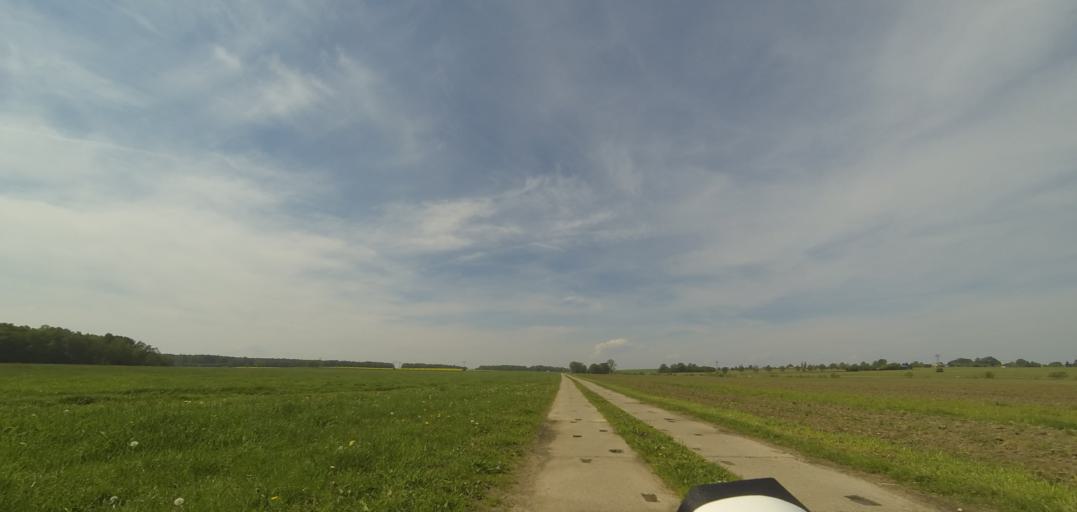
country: DE
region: Saxony
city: Arnsdorf
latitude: 51.0905
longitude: 13.9650
